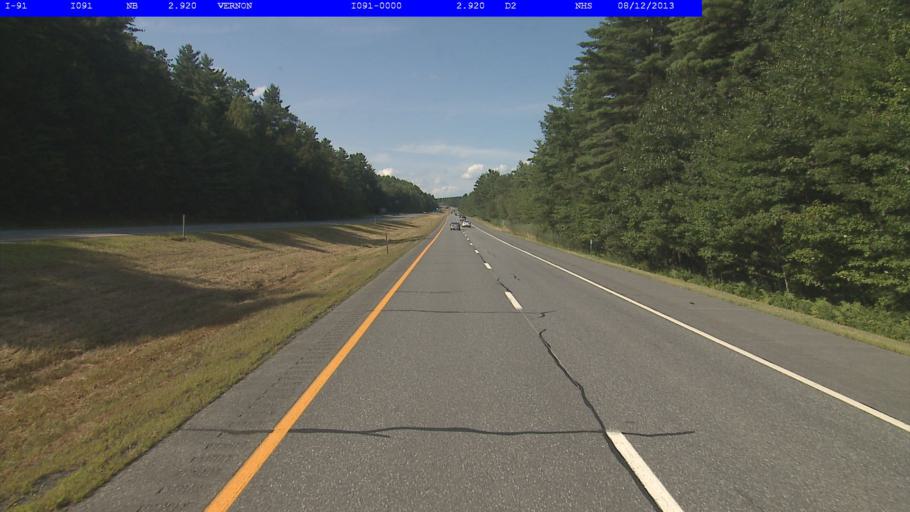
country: US
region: New Hampshire
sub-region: Cheshire County
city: Hinsdale
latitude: 42.7717
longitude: -72.5615
